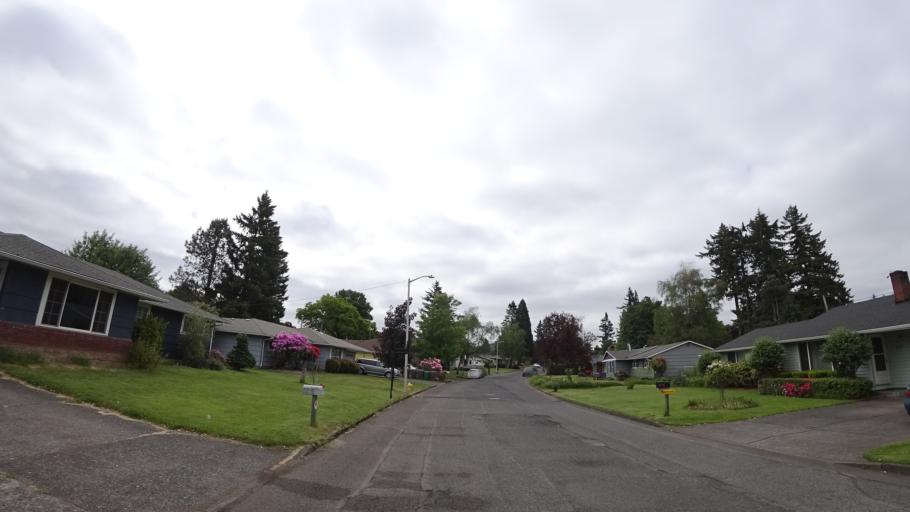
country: US
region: Oregon
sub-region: Multnomah County
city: Gresham
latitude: 45.4994
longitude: -122.4817
